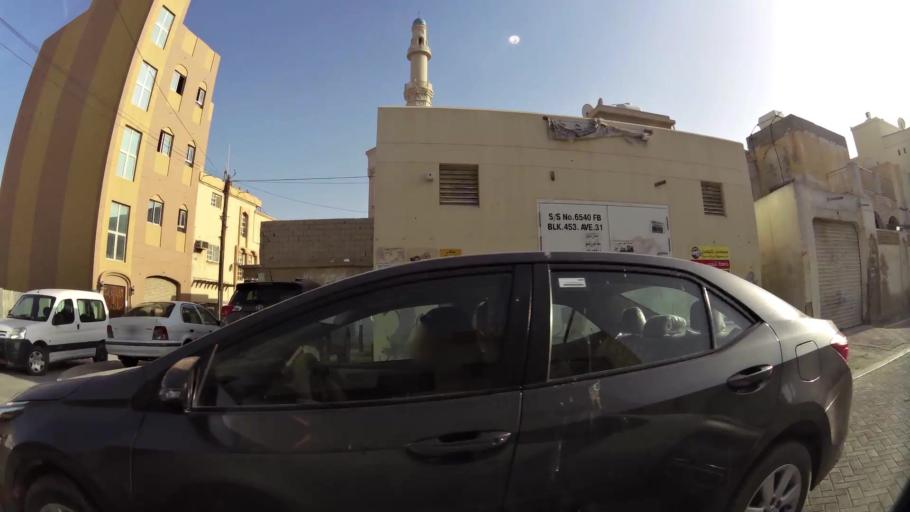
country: BH
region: Manama
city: Jidd Hafs
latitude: 26.2159
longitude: 50.5179
